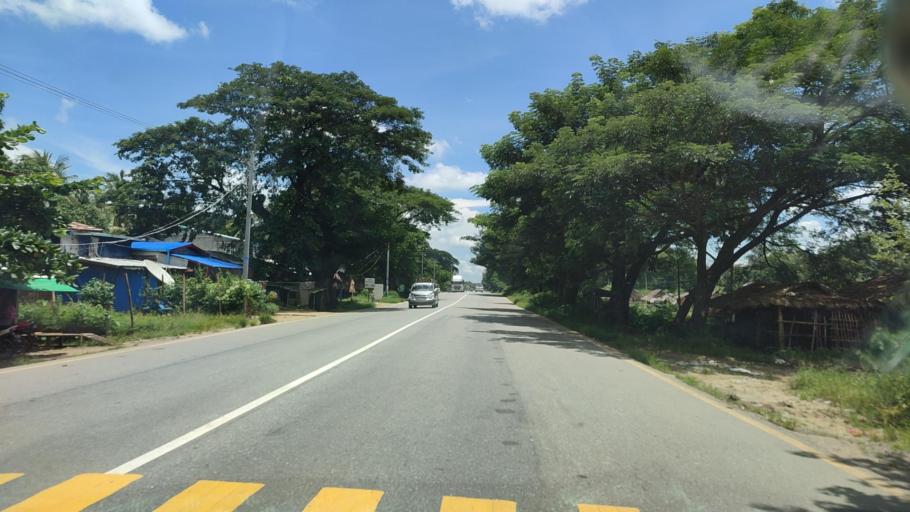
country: MM
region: Bago
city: Pyu
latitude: 18.4076
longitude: 96.4596
